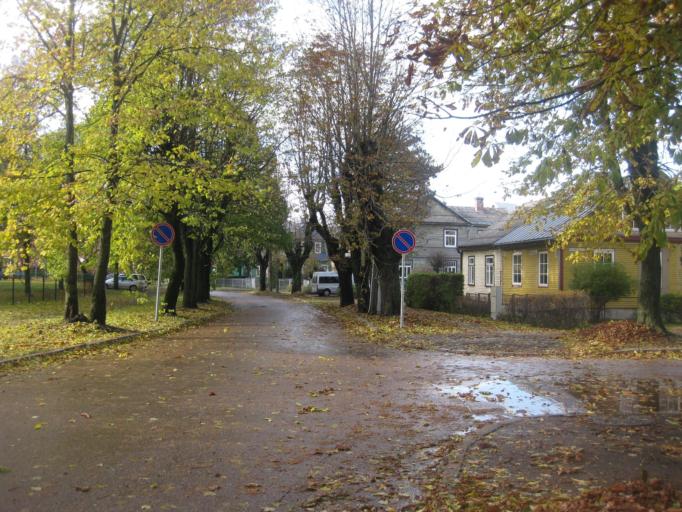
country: LT
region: Kauno apskritis
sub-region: Kaunas
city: Eiguliai
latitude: 54.9031
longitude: 23.9406
